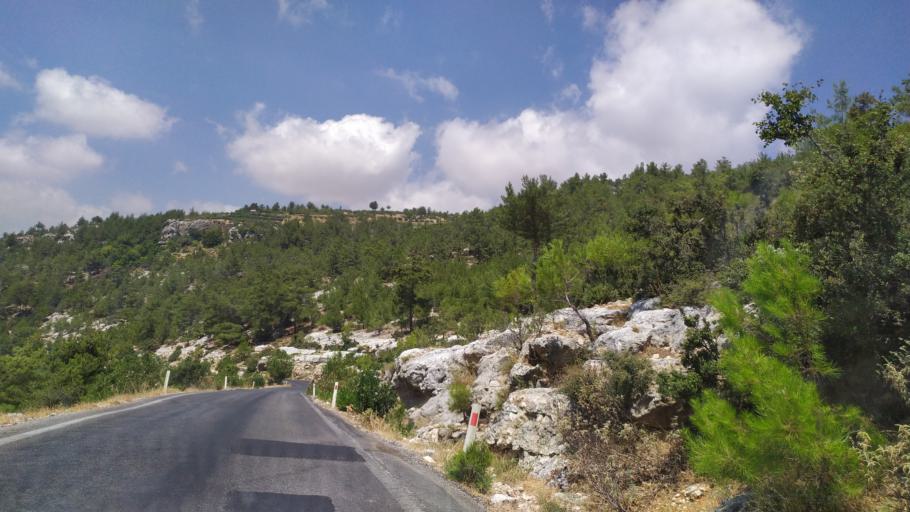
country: TR
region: Mersin
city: Gulnar
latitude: 36.2757
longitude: 33.3833
